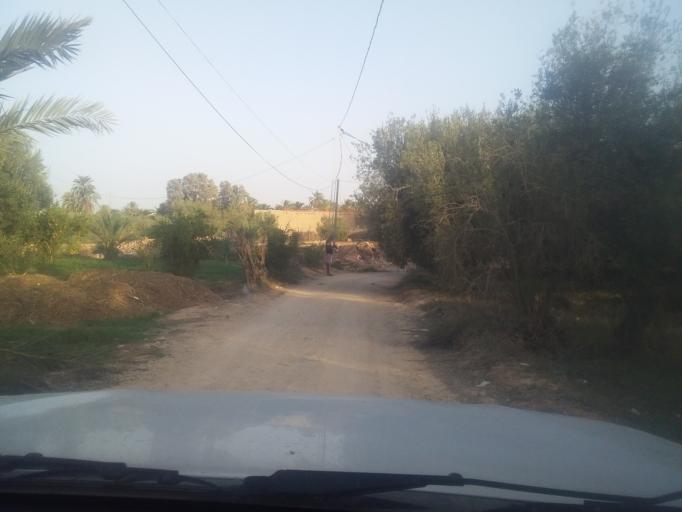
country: TN
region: Qabis
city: Gabes
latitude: 33.6260
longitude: 10.2918
